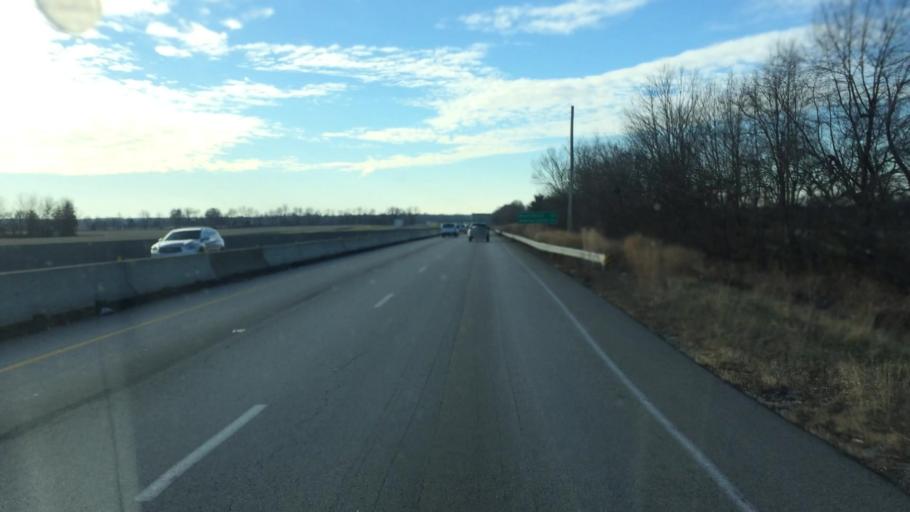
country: US
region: Kentucky
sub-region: Hardin County
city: Elizabethtown
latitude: 37.5835
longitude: -85.8717
